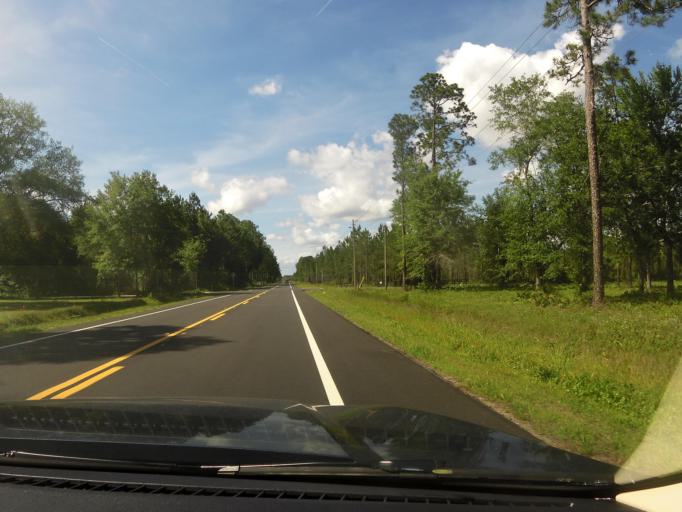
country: US
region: Florida
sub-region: Nassau County
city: Hilliard
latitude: 30.6429
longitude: -81.9030
